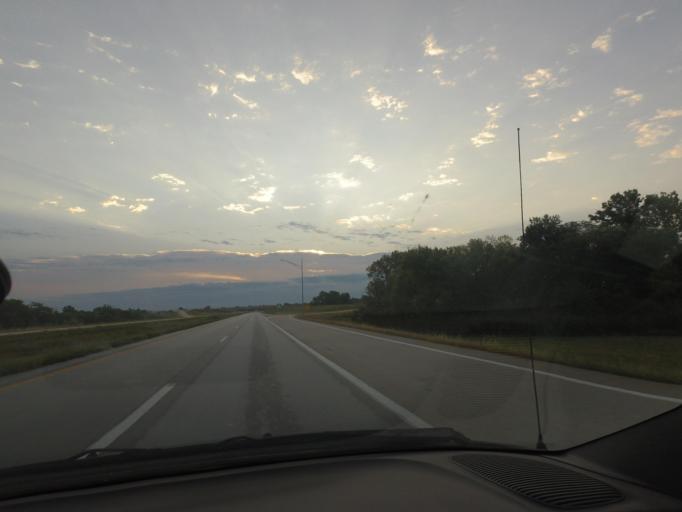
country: US
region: Missouri
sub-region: Macon County
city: Macon
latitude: 39.7514
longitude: -92.2641
